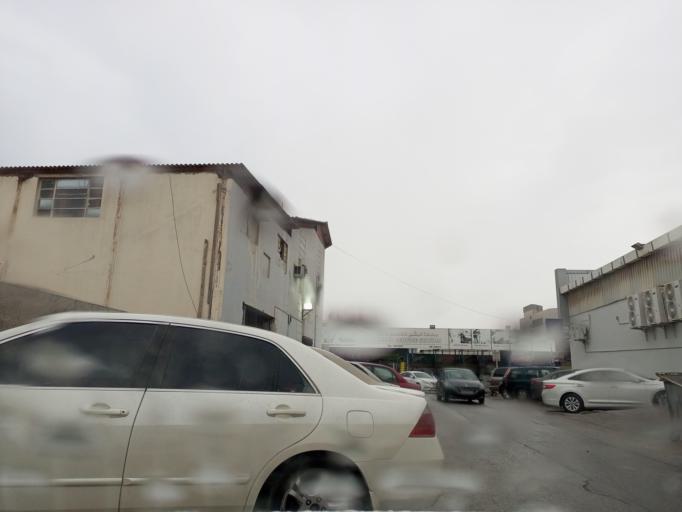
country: BH
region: Muharraq
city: Al Hadd
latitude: 26.2591
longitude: 50.6433
